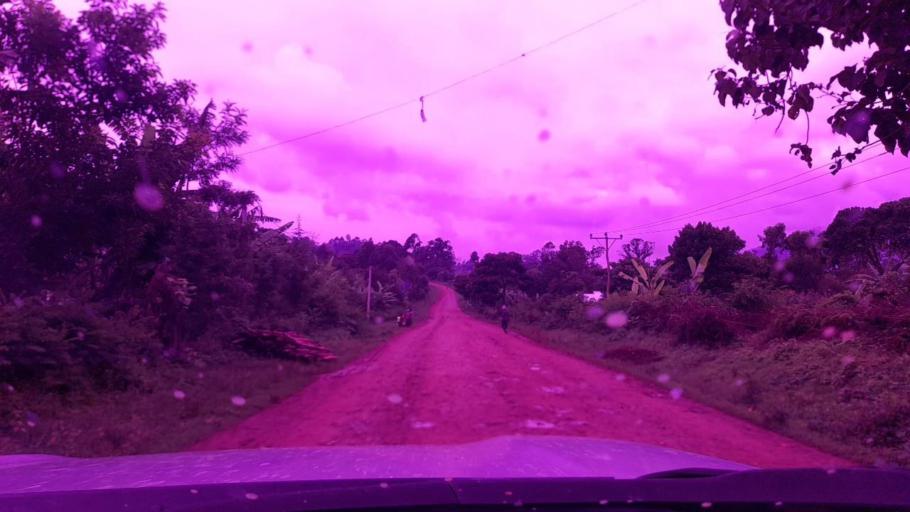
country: ET
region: Southern Nations, Nationalities, and People's Region
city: Bonga
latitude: 7.5528
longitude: 35.8561
